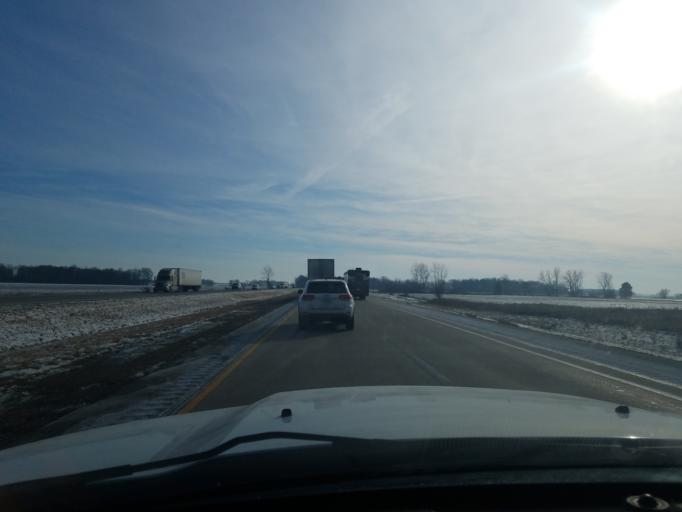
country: US
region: Indiana
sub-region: Huntington County
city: Markle
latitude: 40.7851
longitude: -85.3838
